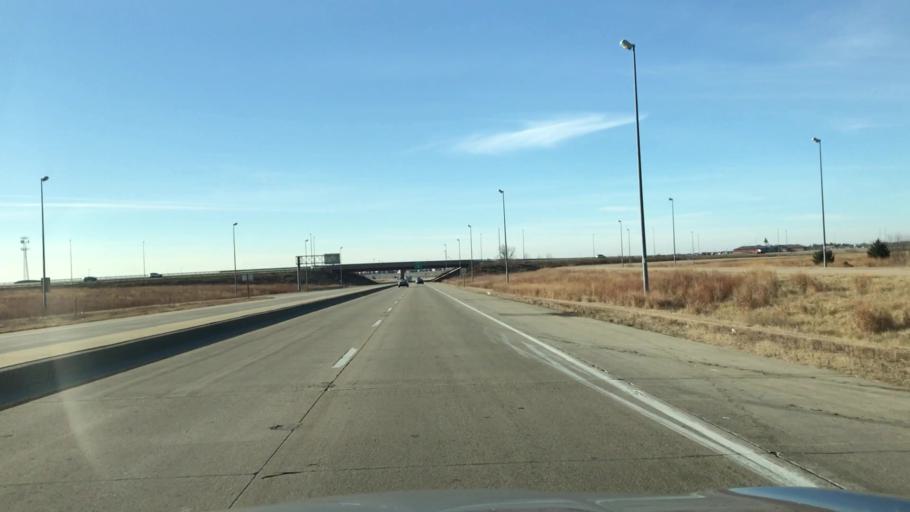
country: US
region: Illinois
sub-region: McLean County
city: Normal
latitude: 40.5404
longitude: -88.9458
